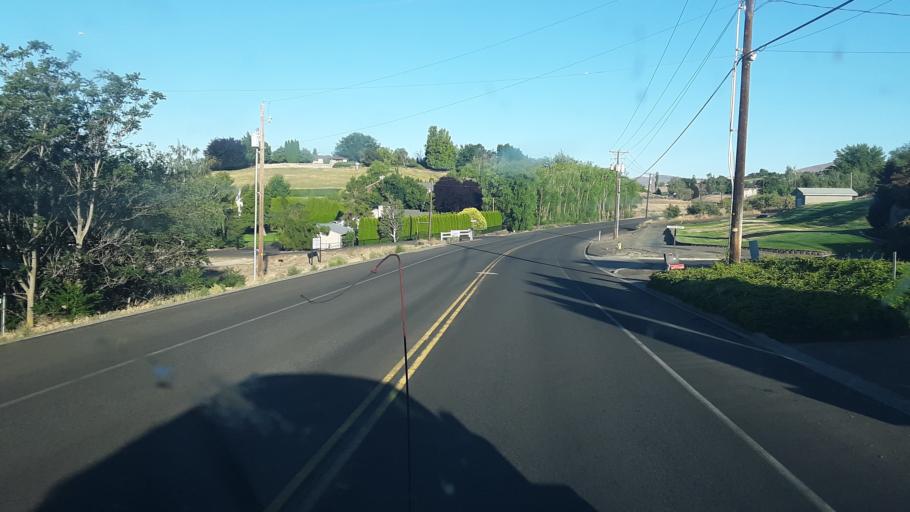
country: US
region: Washington
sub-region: Yakima County
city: West Valley
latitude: 46.6003
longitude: -120.6430
